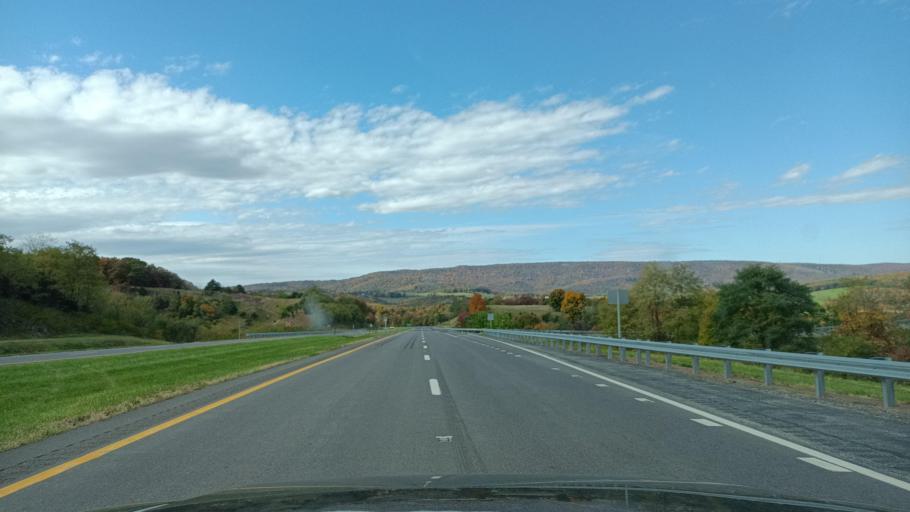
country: US
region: West Virginia
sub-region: Hardy County
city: Moorefield
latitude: 39.0953
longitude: -78.8077
